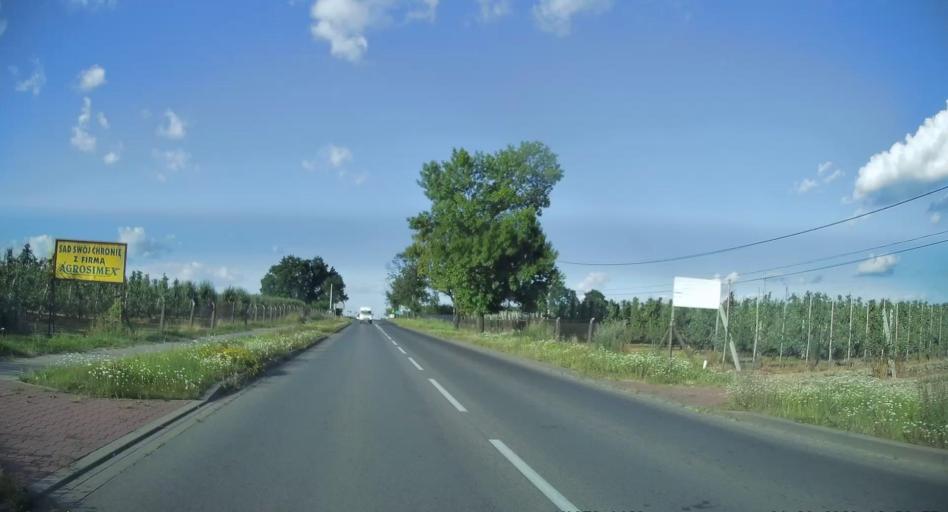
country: PL
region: Masovian Voivodeship
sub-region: Powiat grojecki
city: Belsk Duzy
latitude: 51.8348
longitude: 20.8209
